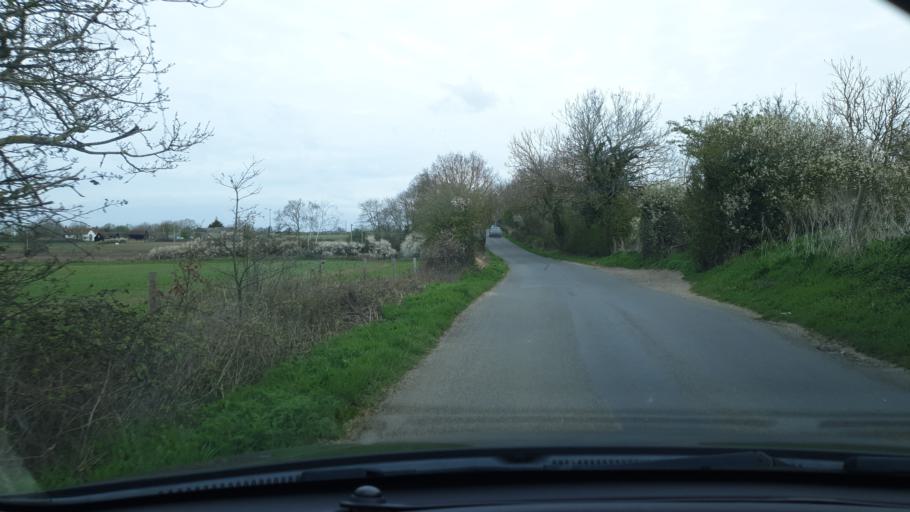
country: GB
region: England
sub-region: Essex
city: Great Bentley
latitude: 51.8514
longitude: 1.0866
